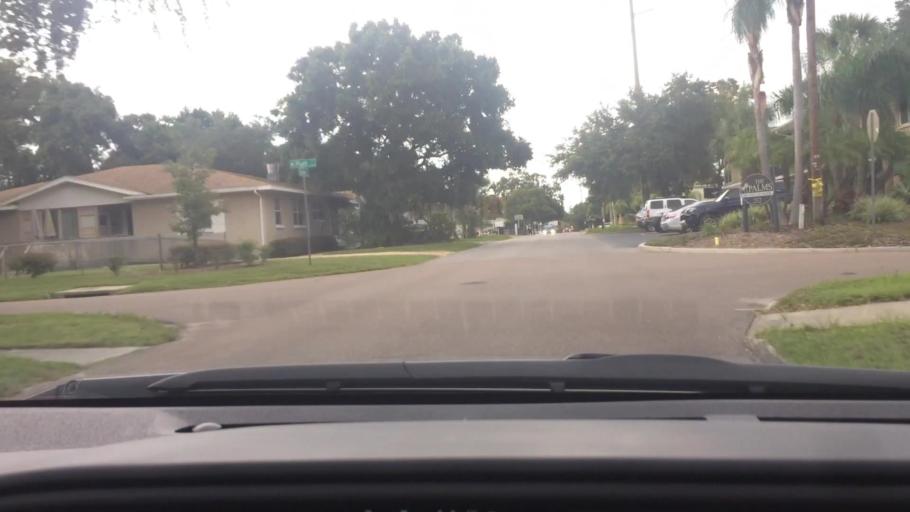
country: US
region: Florida
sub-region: Hillsborough County
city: Tampa
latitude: 27.9420
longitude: -82.5079
